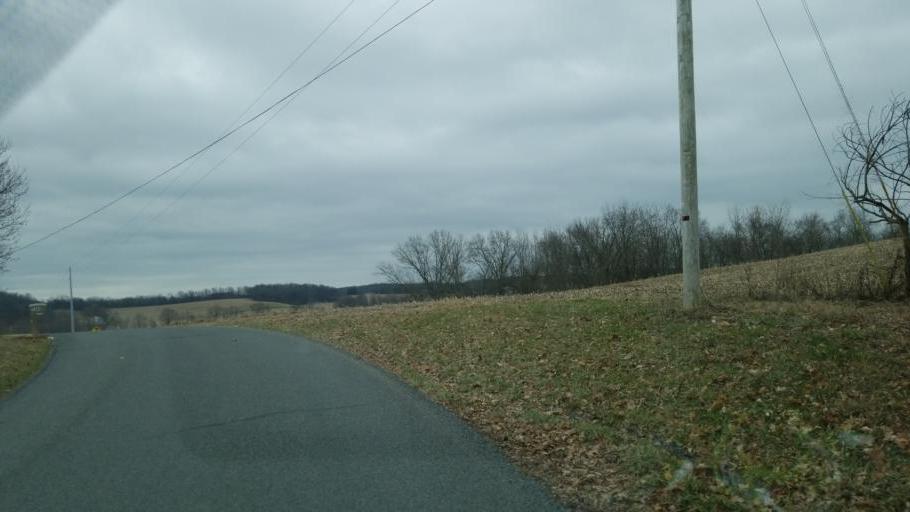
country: US
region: Ohio
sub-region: Licking County
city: Utica
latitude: 40.1984
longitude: -82.4041
